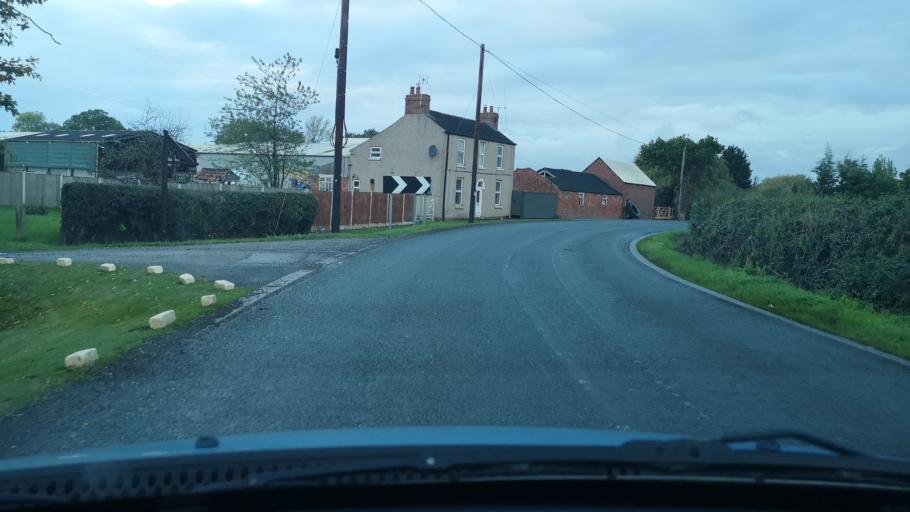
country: GB
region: England
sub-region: Doncaster
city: Moss
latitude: 53.6165
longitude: -1.0658
